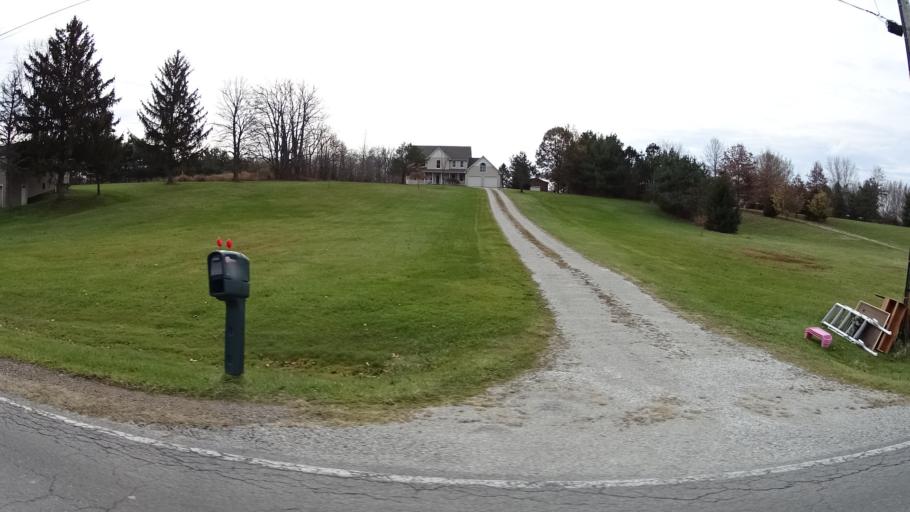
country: US
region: Ohio
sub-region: Lorain County
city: Lagrange
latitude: 41.1365
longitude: -82.0960
